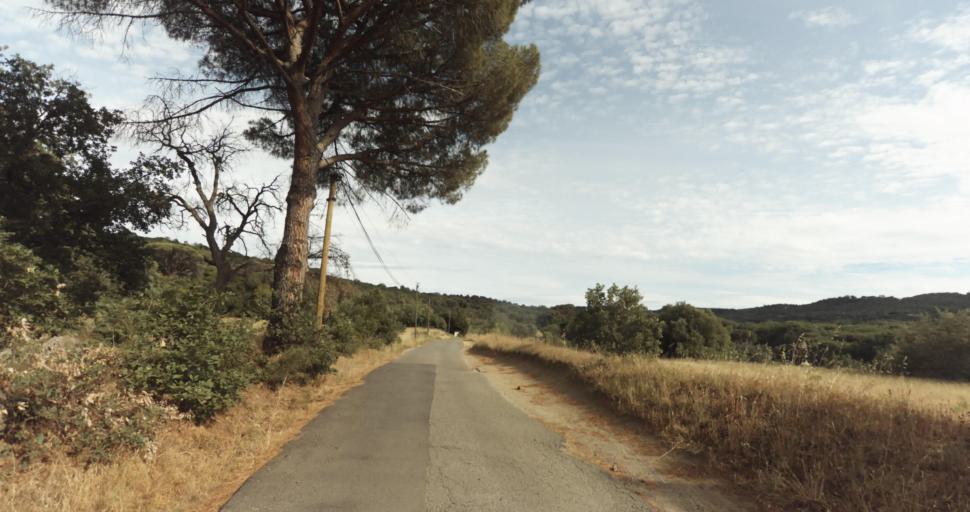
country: FR
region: Provence-Alpes-Cote d'Azur
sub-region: Departement du Var
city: Gassin
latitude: 43.2239
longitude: 6.5790
